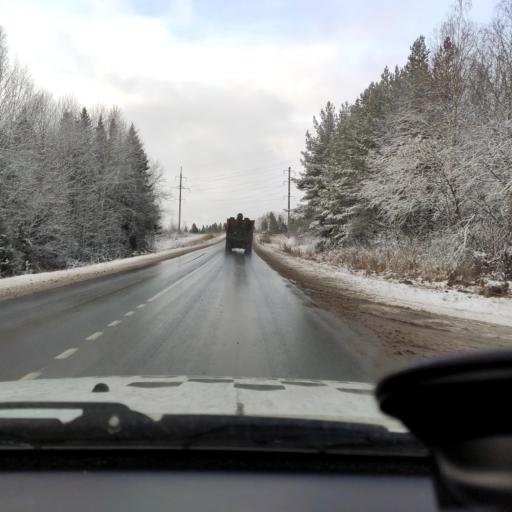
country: RU
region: Perm
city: Nytva
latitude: 57.9360
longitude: 55.3781
